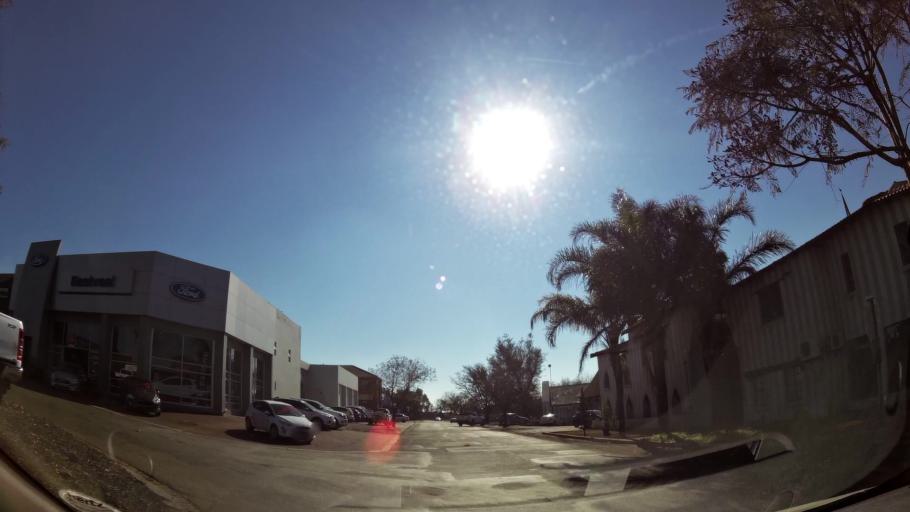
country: ZA
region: Mpumalanga
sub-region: Nkangala District Municipality
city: Witbank
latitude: -25.8752
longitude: 29.2402
